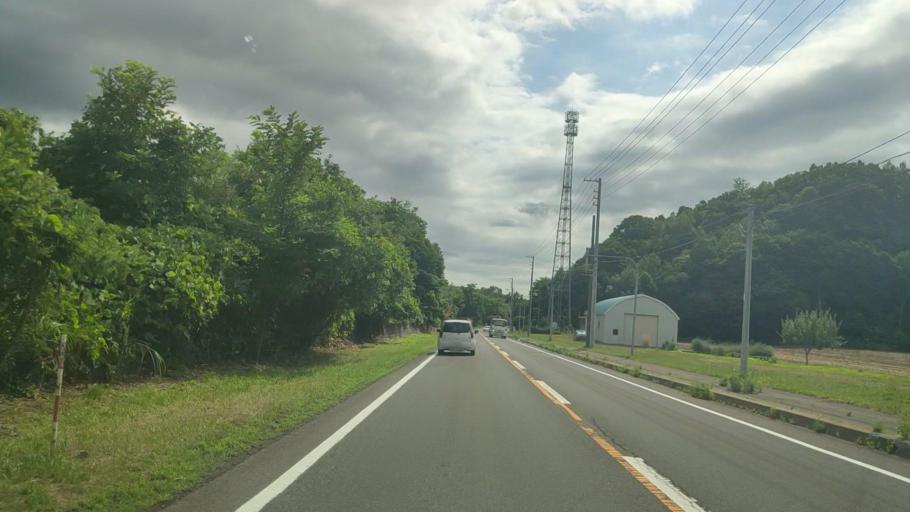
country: JP
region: Hokkaido
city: Date
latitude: 42.5695
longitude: 140.9240
